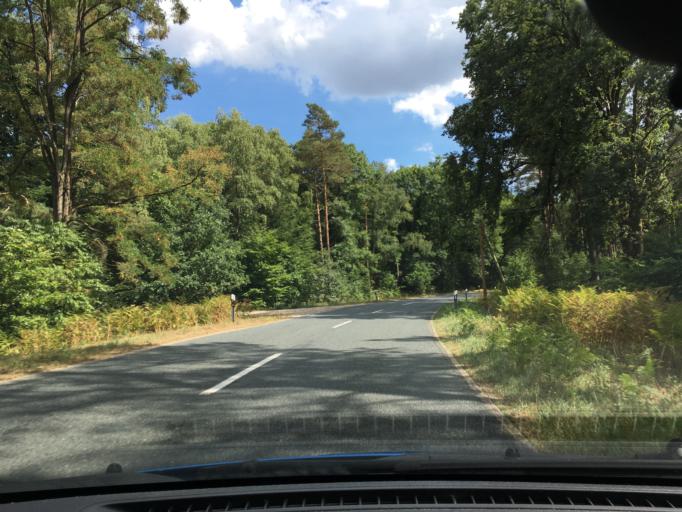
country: DE
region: Lower Saxony
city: Rehlingen
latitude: 53.0799
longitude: 10.2260
